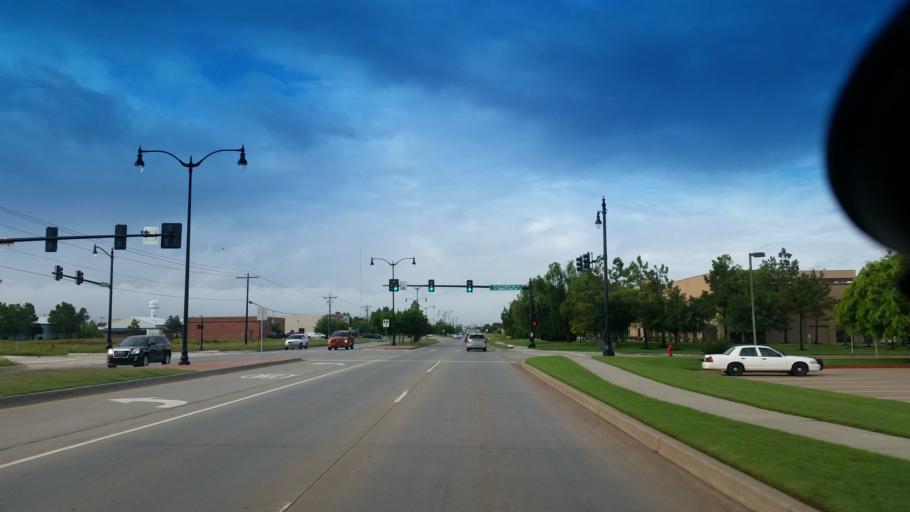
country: US
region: Oklahoma
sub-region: Oklahoma County
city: Edmond
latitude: 35.6340
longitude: -97.4962
